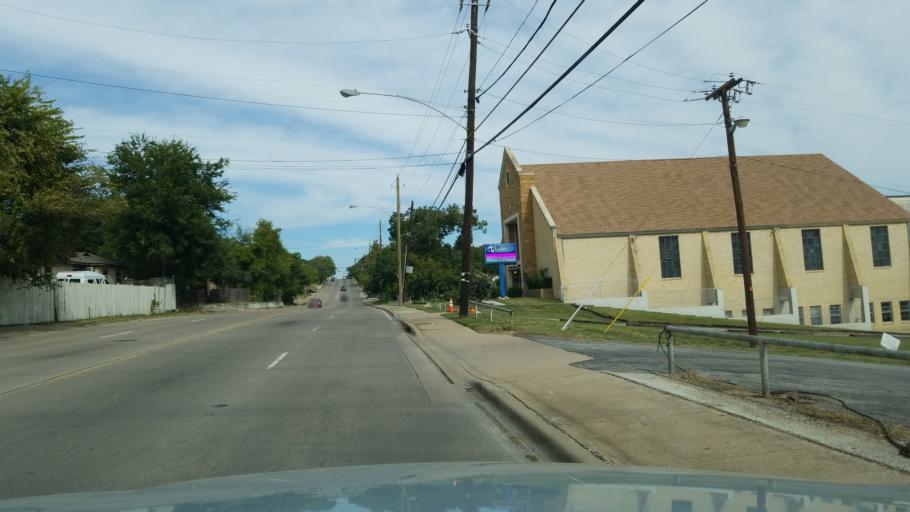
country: US
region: Texas
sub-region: Dallas County
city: Dallas
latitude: 32.7867
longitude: -96.7374
